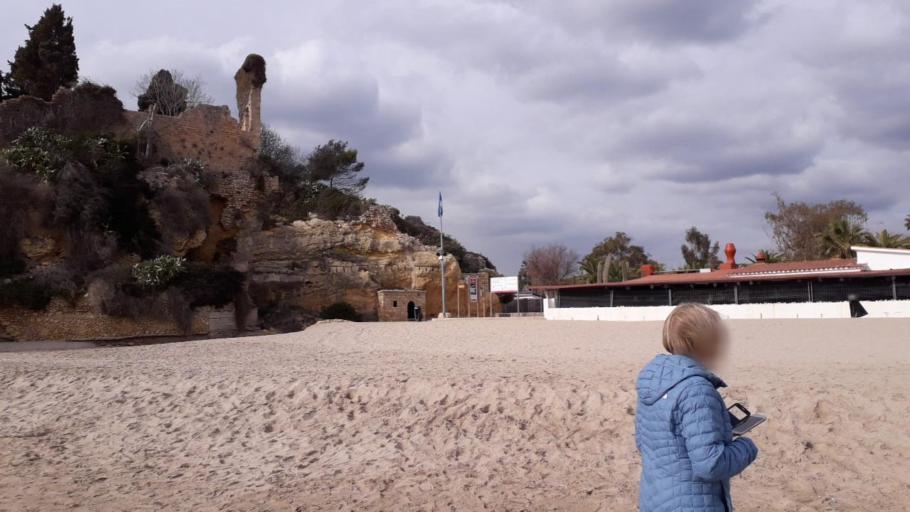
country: ES
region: Catalonia
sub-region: Provincia de Tarragona
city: Altafulla
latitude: 41.1303
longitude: 1.3621
